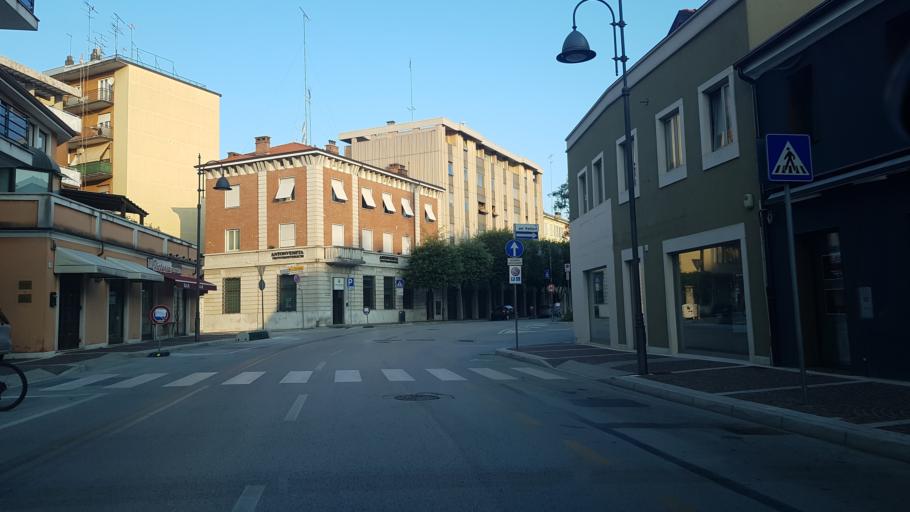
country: IT
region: Friuli Venezia Giulia
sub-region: Provincia di Gorizia
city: Monfalcone
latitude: 45.8076
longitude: 13.5342
